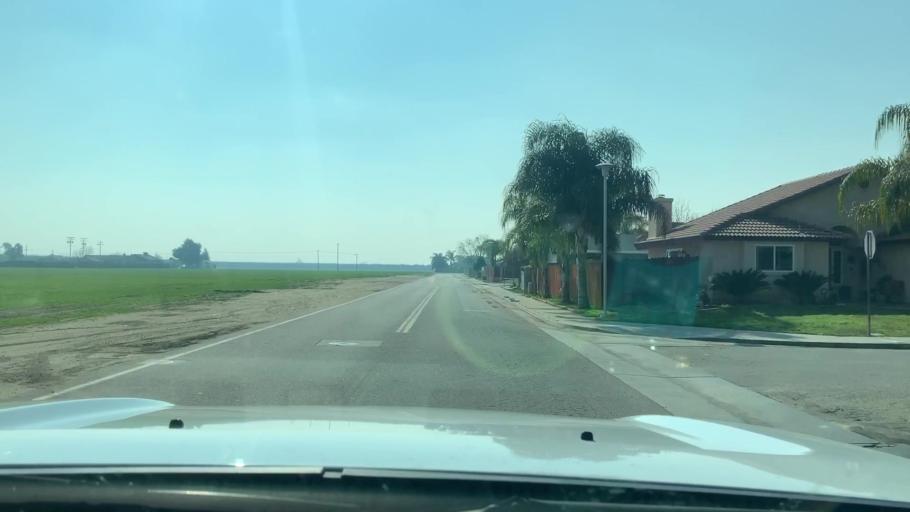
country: US
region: California
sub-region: Kern County
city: Shafter
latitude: 35.4956
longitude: -119.2739
